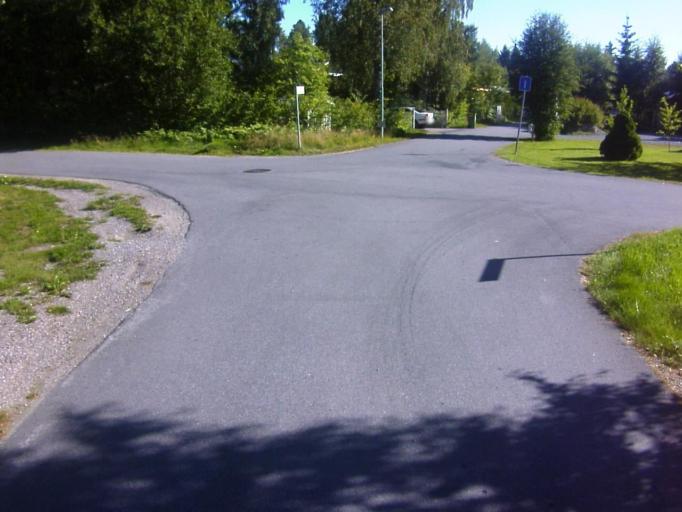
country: SE
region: Soedermanland
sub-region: Eskilstuna Kommun
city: Hallbybrunn
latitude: 59.3368
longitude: 16.4174
